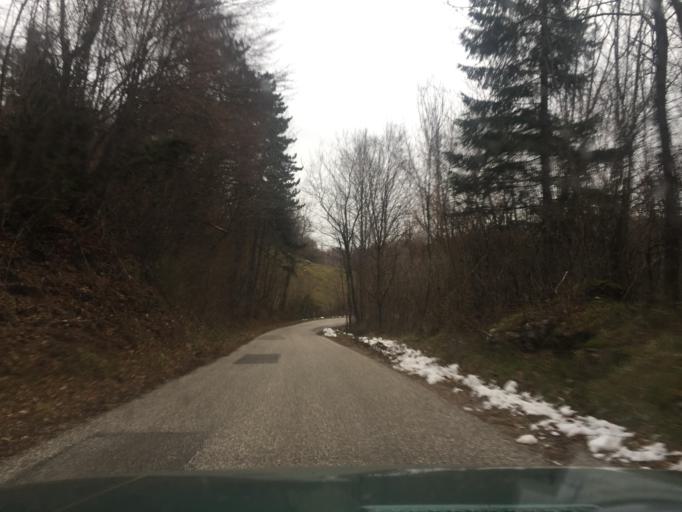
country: SI
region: Kanal
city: Kanal
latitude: 46.0676
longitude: 13.6632
